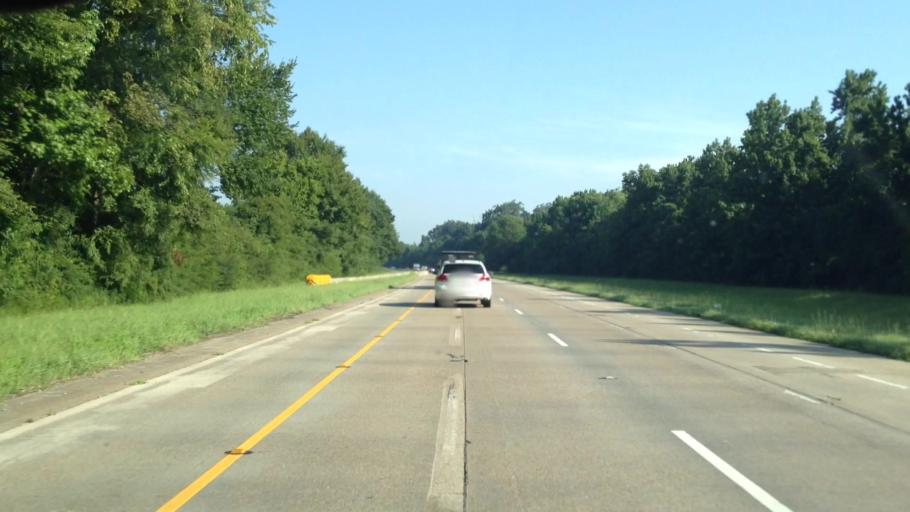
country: US
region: Louisiana
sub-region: Ascension Parish
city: Prairieville
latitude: 30.3129
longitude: -90.9971
